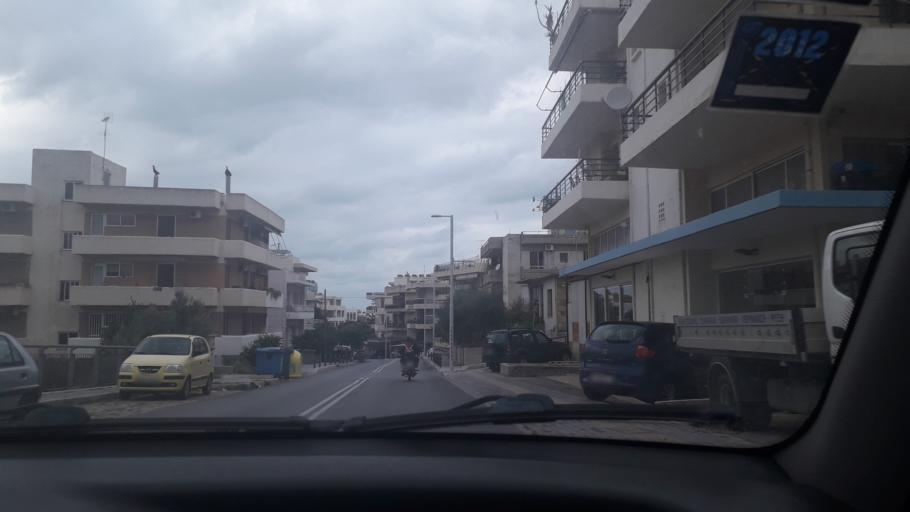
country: GR
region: Crete
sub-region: Nomos Rethymnis
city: Rethymno
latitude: 35.3605
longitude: 24.4744
